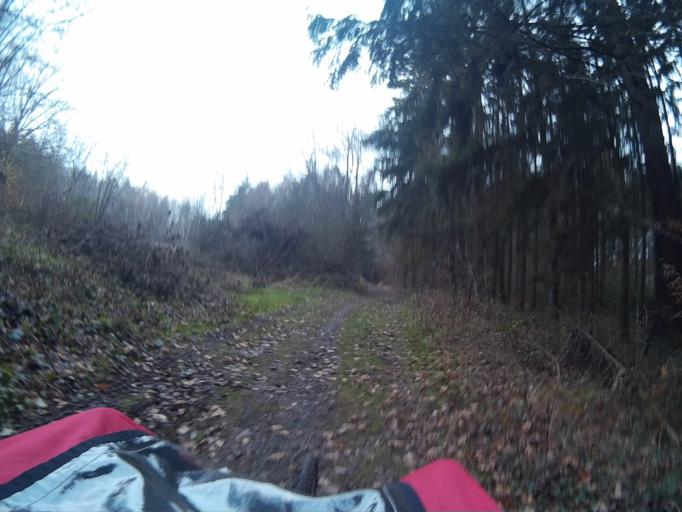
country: CZ
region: Plzensky
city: Stary Plzenec
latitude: 49.6824
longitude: 13.4775
